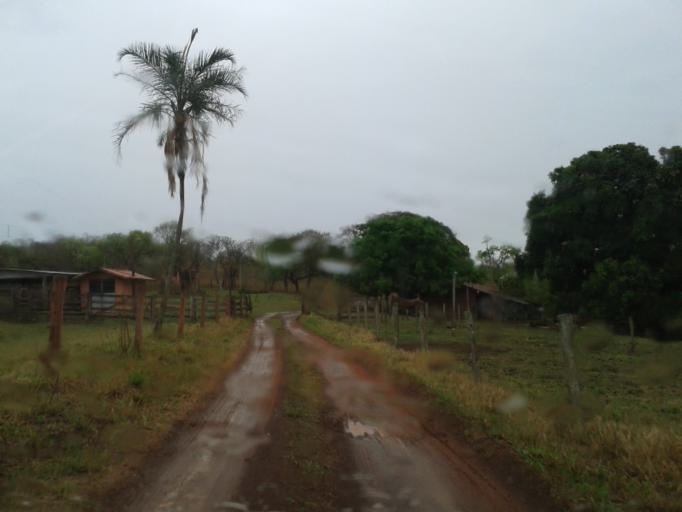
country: BR
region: Minas Gerais
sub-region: Campina Verde
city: Campina Verde
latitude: -19.3123
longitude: -49.5084
